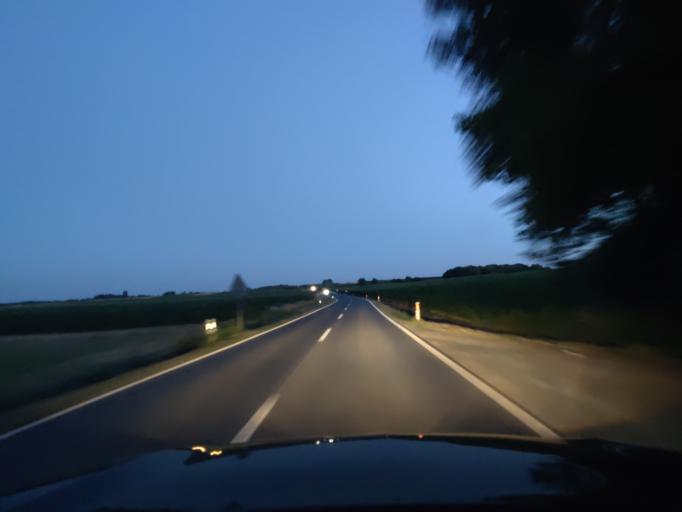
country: HR
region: Medimurska
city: Vratisinec
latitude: 46.4855
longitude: 16.4255
